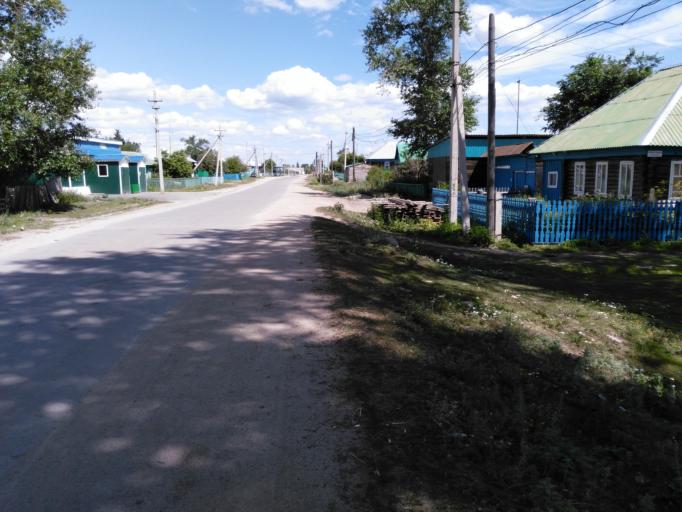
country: RU
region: Bashkortostan
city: Akhunovo
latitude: 54.2043
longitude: 59.5906
